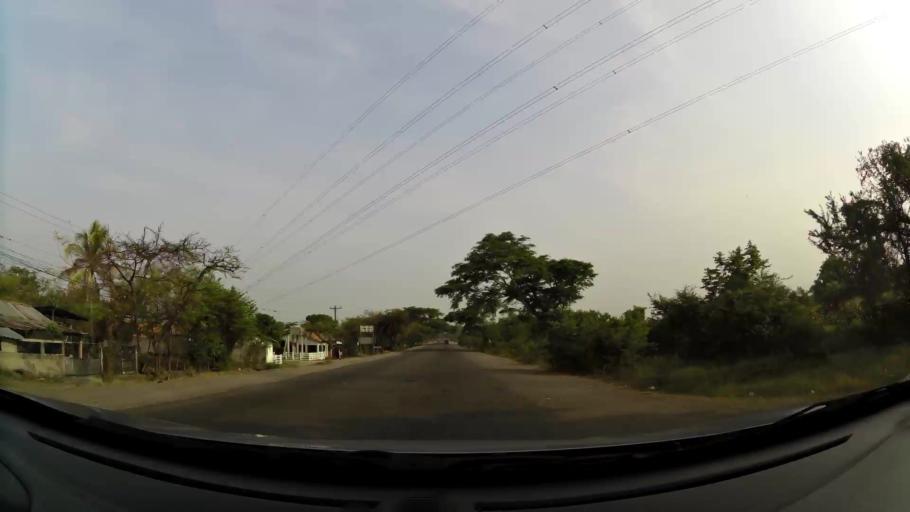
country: HN
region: Comayagua
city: Flores
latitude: 14.2834
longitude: -87.5660
